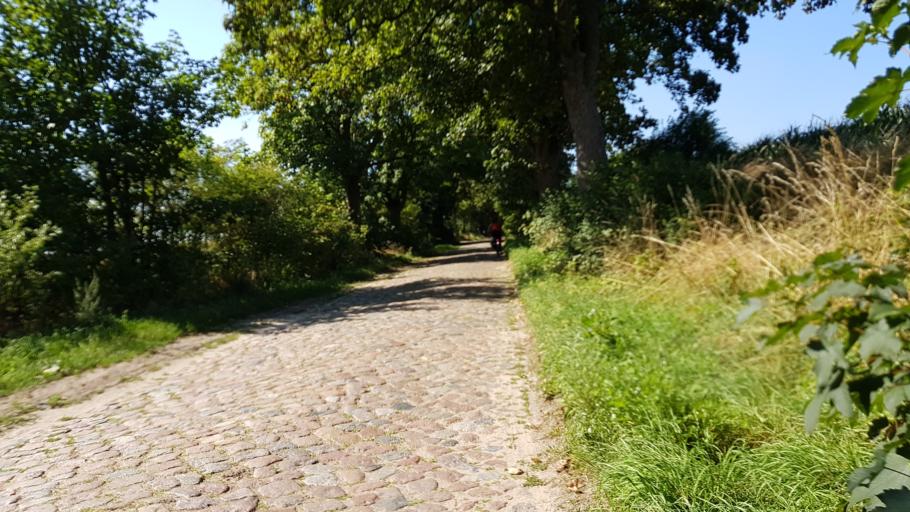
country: PL
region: West Pomeranian Voivodeship
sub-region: Powiat gryfinski
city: Gryfino
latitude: 53.1518
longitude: 14.5031
